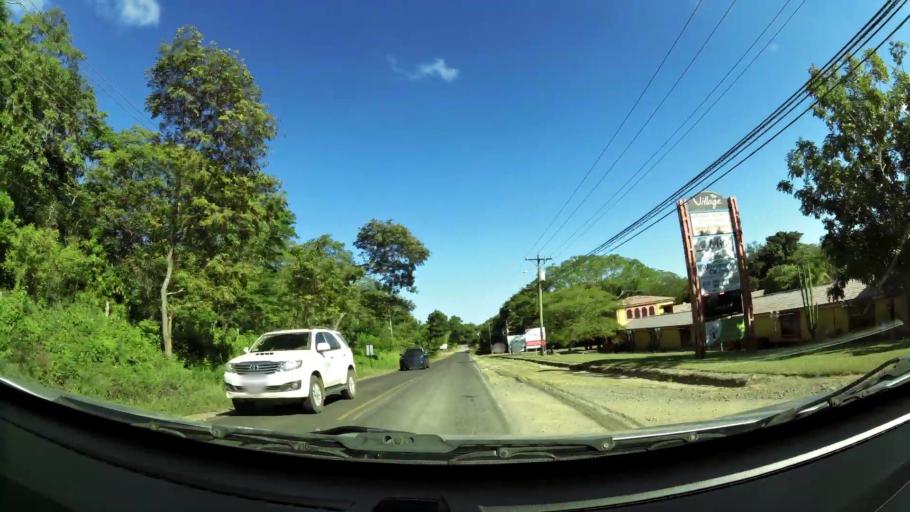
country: CR
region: Guanacaste
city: Sardinal
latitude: 10.3932
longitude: -85.7912
